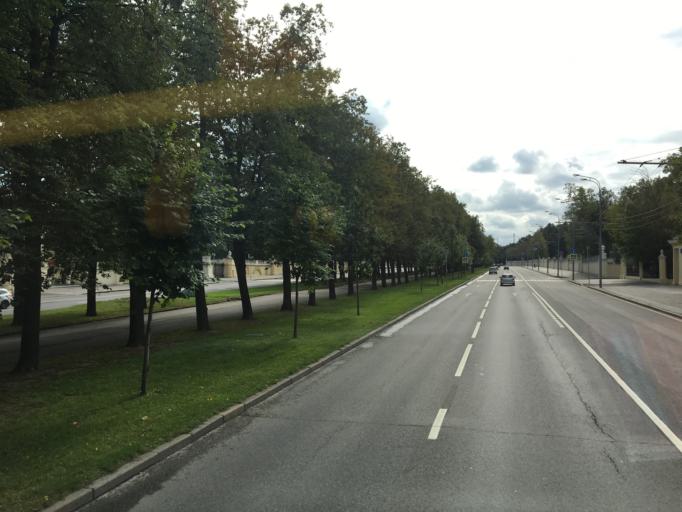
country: RU
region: Moscow
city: Vorob'yovo
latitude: 55.7217
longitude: 37.5349
